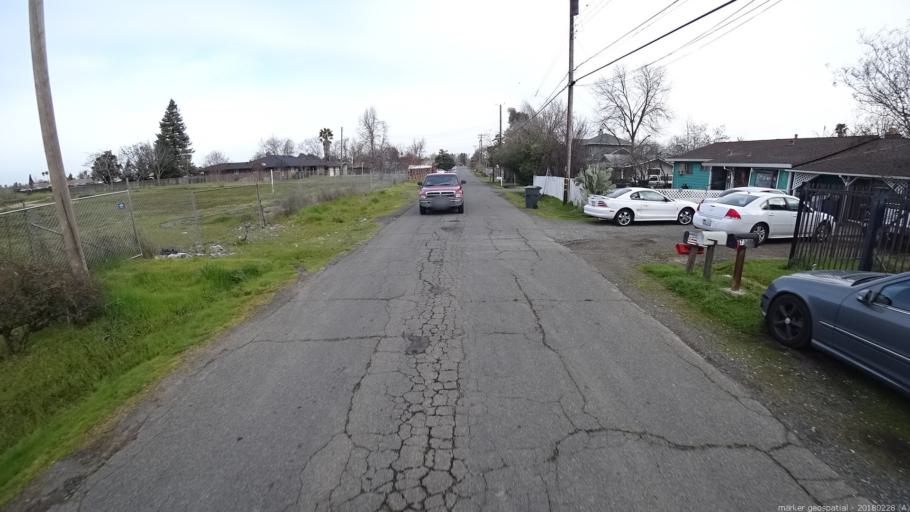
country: US
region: California
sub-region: Sacramento County
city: Rio Linda
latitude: 38.7004
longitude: -121.4523
